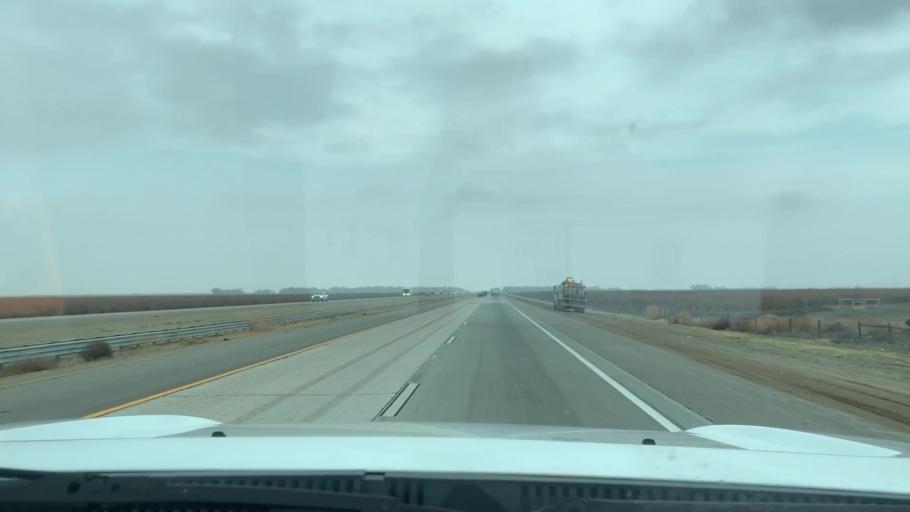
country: US
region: California
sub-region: Kern County
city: Lost Hills
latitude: 35.5771
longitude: -119.6176
